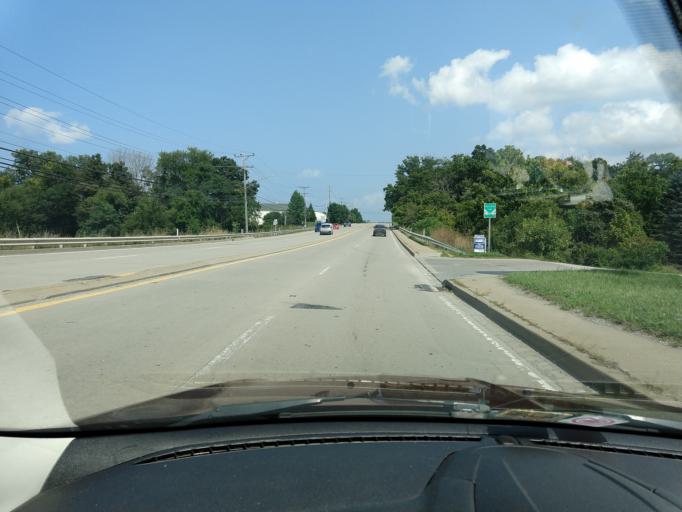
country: US
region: Pennsylvania
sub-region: Greene County
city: Morrisville
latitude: 39.8973
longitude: -80.1596
